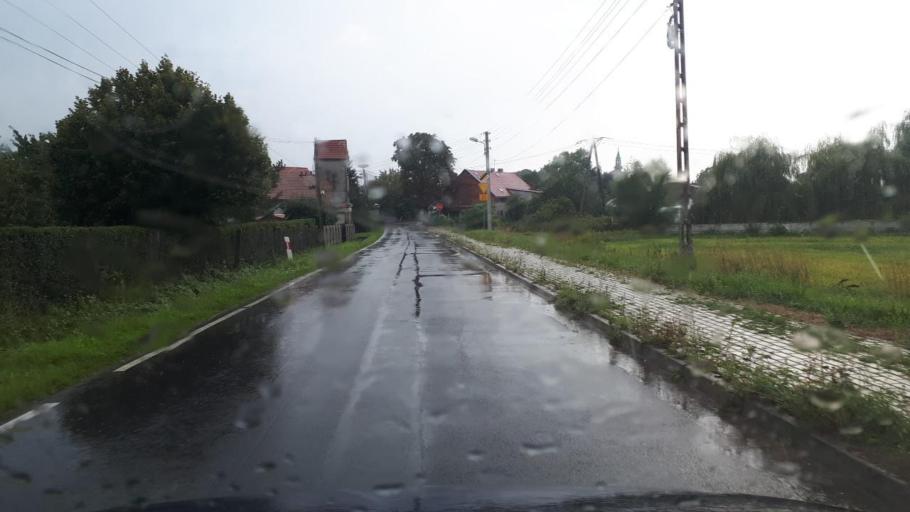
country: PL
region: Silesian Voivodeship
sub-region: Powiat gliwicki
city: Wielowies
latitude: 50.5123
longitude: 18.6221
